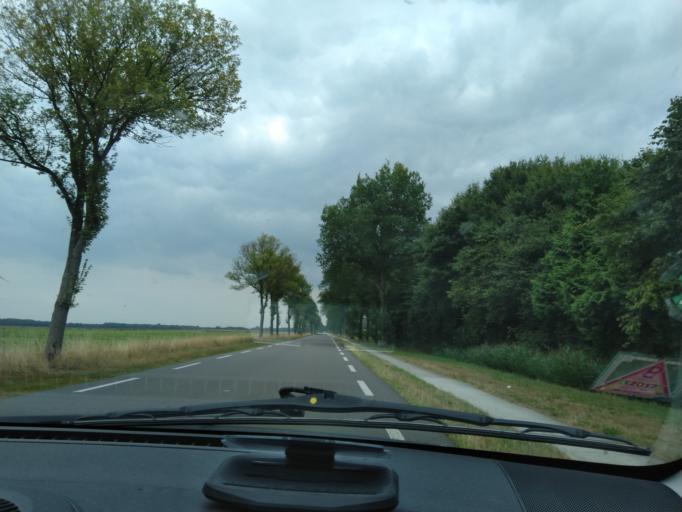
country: NL
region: Groningen
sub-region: Gemeente Vlagtwedde
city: Vlagtwedde
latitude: 53.0846
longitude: 7.1756
